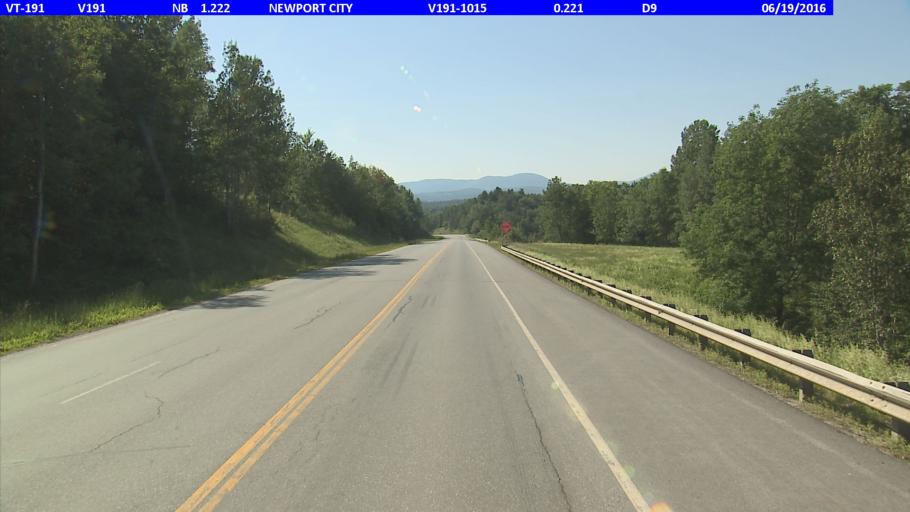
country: US
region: Vermont
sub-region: Orleans County
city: Newport
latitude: 44.9345
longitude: -72.1854
